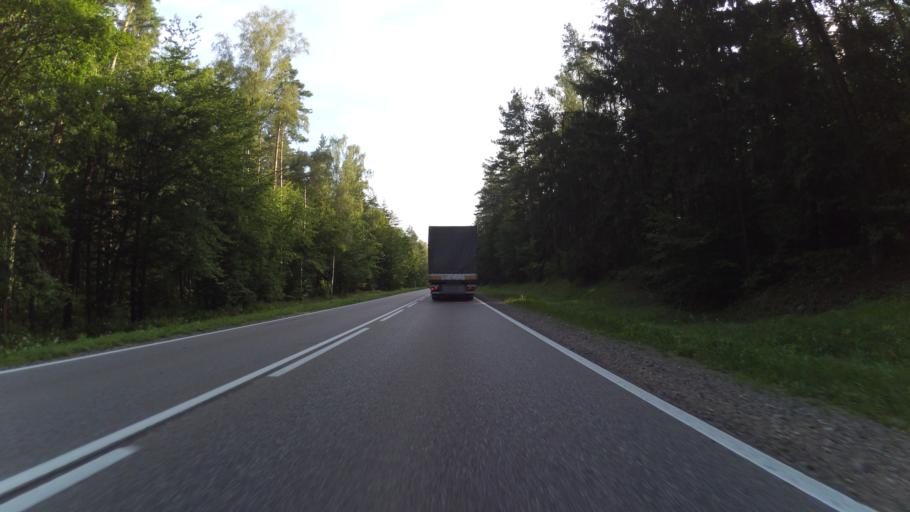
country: PL
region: Podlasie
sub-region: Powiat bialostocki
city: Czarna Bialostocka
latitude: 53.2653
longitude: 23.2601
